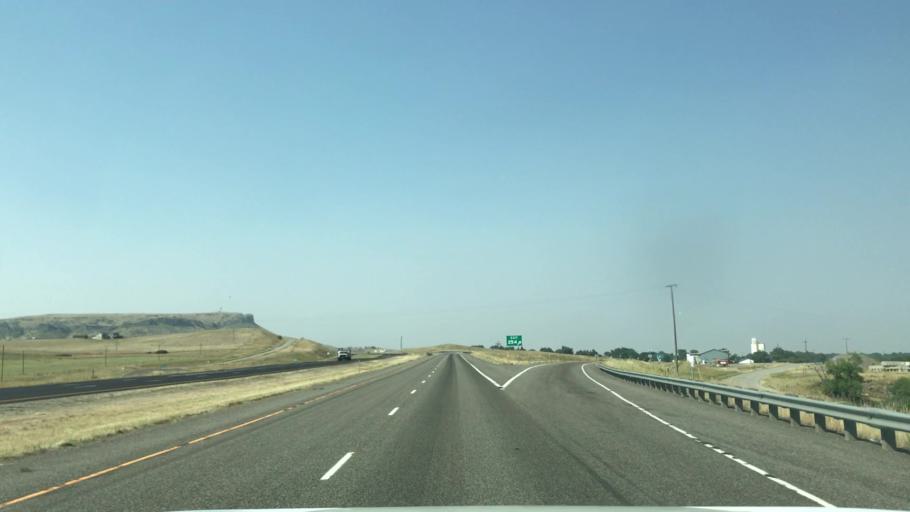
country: US
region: Montana
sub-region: Cascade County
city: Sun Prairie
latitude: 47.2569
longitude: -111.7089
